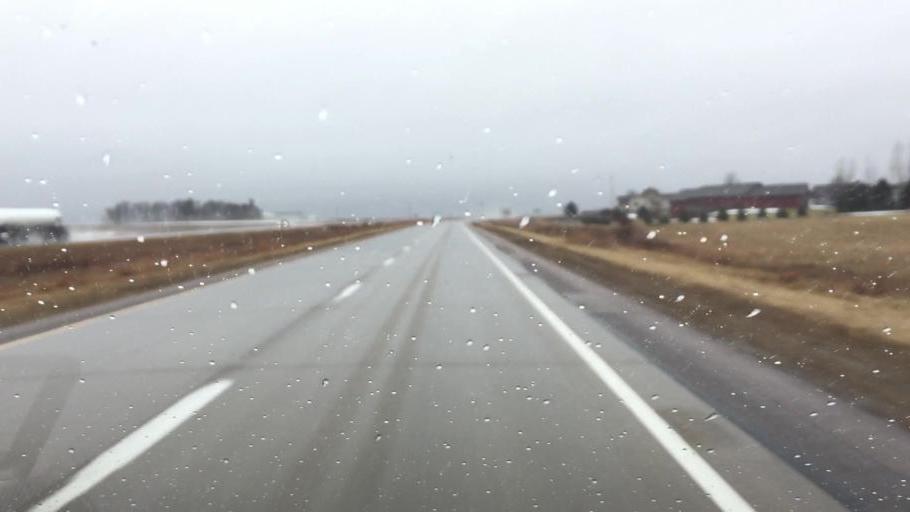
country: US
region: Iowa
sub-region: O'Brien County
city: Sheldon
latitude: 43.0749
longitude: -95.8981
